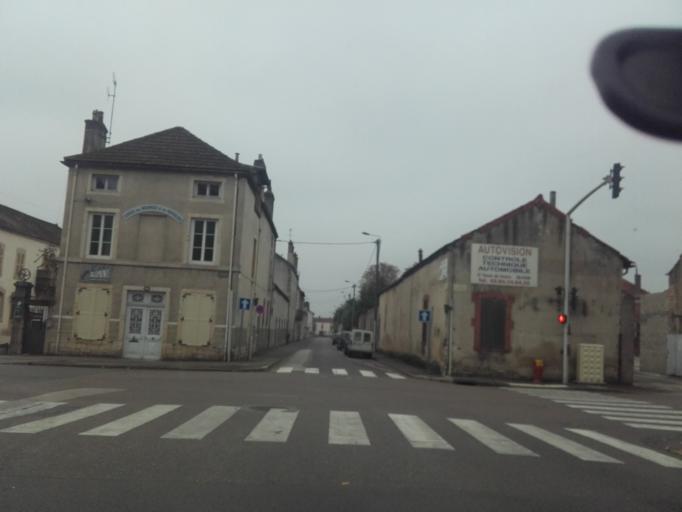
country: FR
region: Bourgogne
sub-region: Departement de la Cote-d'Or
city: Beaune
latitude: 47.0219
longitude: 4.8470
